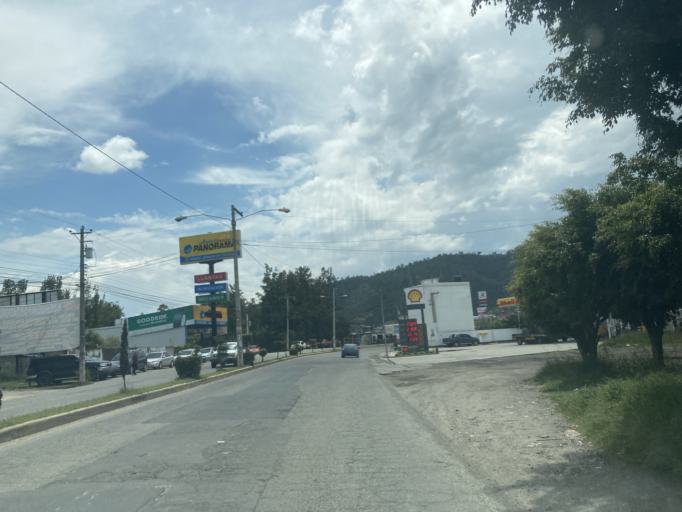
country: GT
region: Huehuetenango
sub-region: Municipio de Huehuetenango
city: Huehuetenango
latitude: 15.3027
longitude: -91.4926
